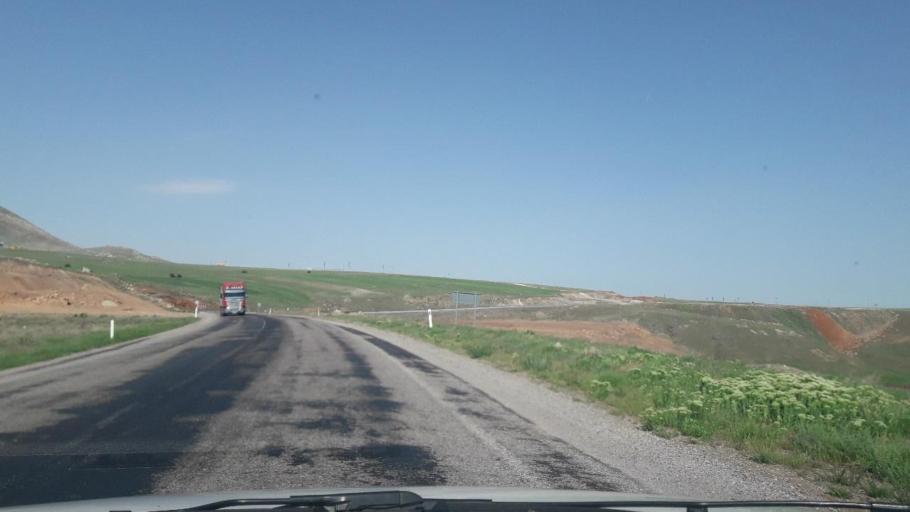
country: TR
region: Sivas
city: Kangal
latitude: 39.1663
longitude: 37.4769
